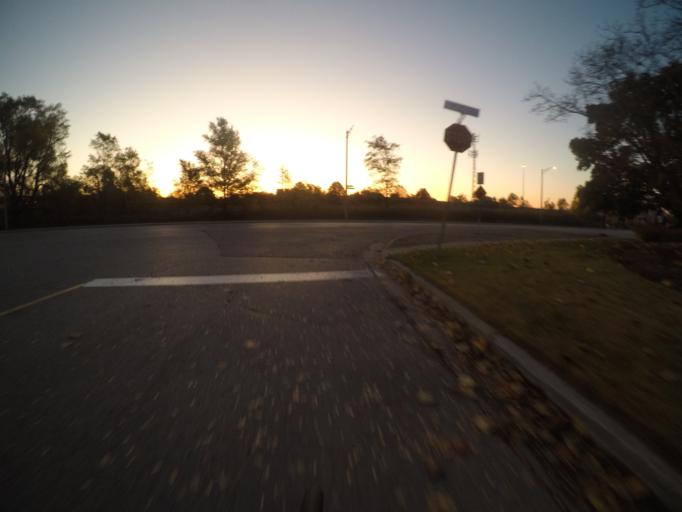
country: CA
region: Ontario
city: Kitchener
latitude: 43.4358
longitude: -80.4592
